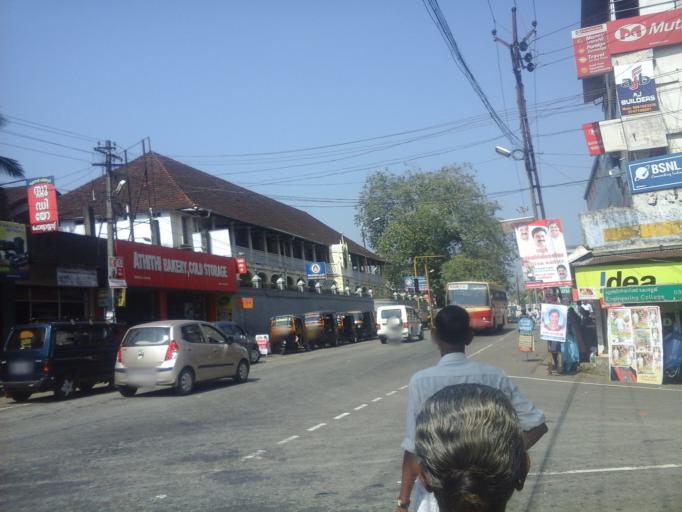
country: IN
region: Kerala
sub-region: Kottayam
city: Lalam
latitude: 9.6998
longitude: 76.7280
